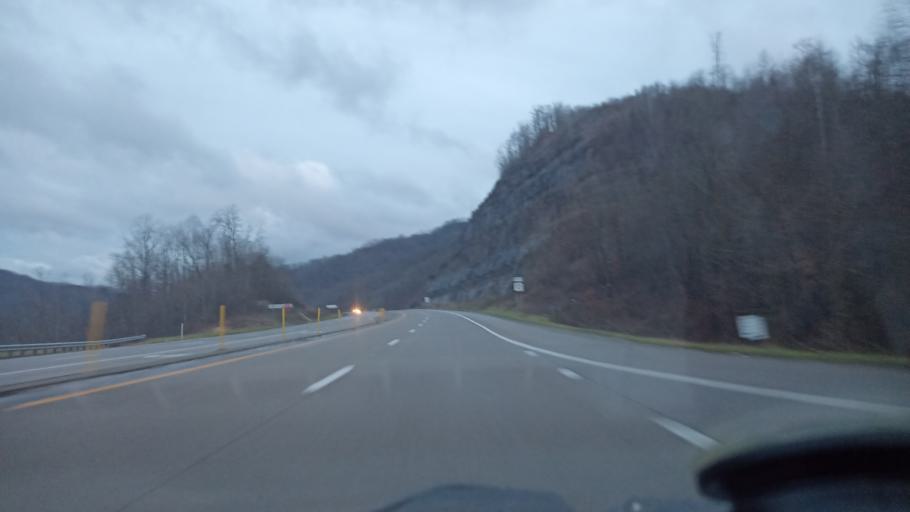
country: US
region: West Virginia
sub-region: Logan County
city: Mallory
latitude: 37.7683
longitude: -81.9221
